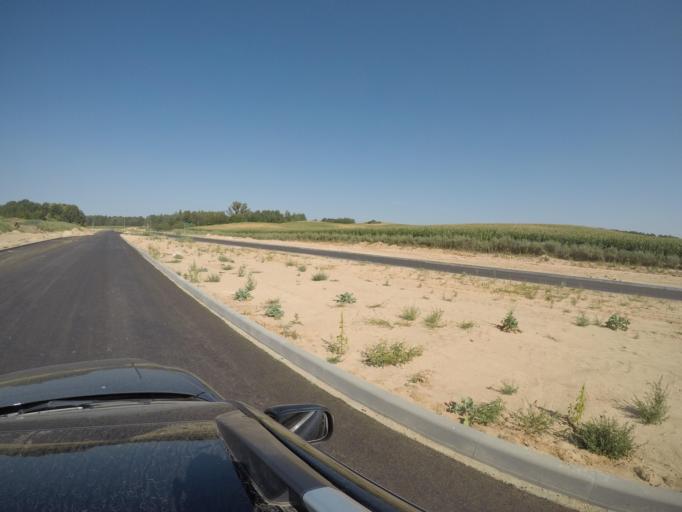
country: BY
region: Grodnenskaya
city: Hrodna
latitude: 53.7245
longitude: 23.8822
